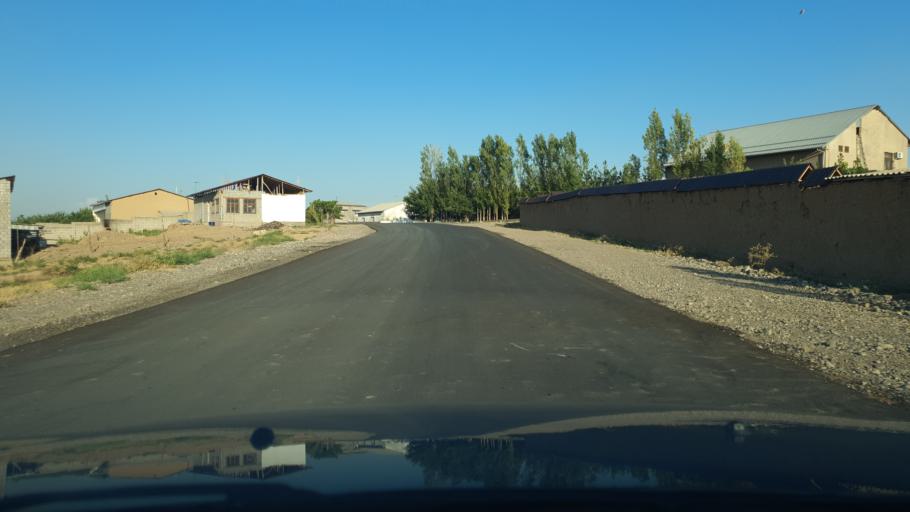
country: UZ
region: Toshkent
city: Salor
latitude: 41.4569
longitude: 69.3972
